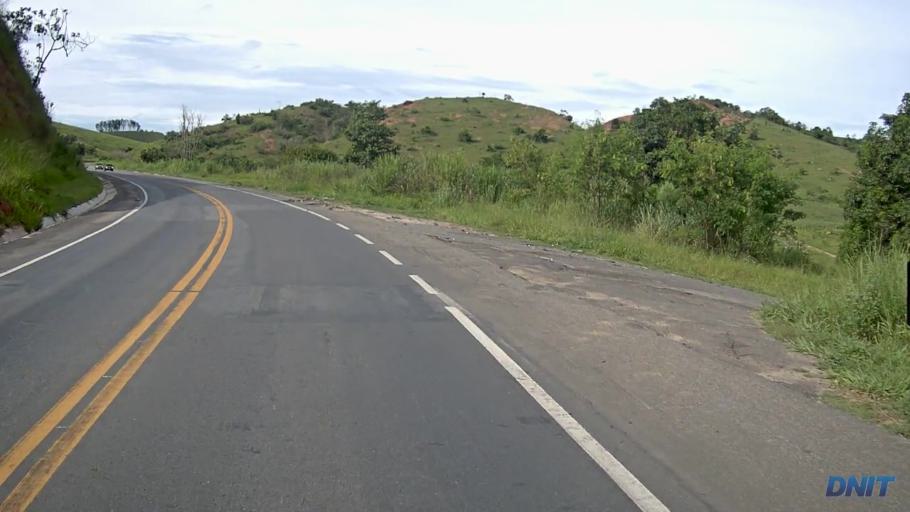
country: BR
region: Minas Gerais
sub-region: Belo Oriente
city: Belo Oriente
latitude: -19.2168
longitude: -42.3066
